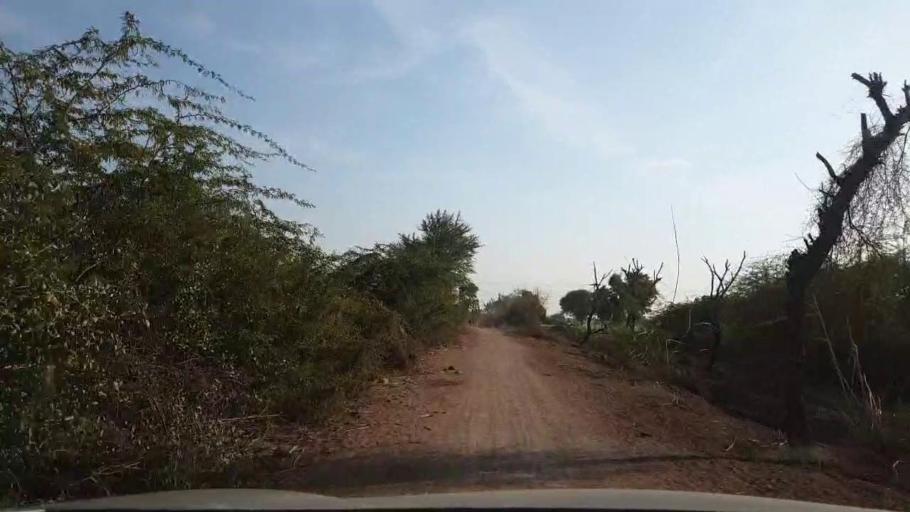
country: PK
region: Sindh
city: Berani
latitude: 25.7311
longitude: 68.7987
